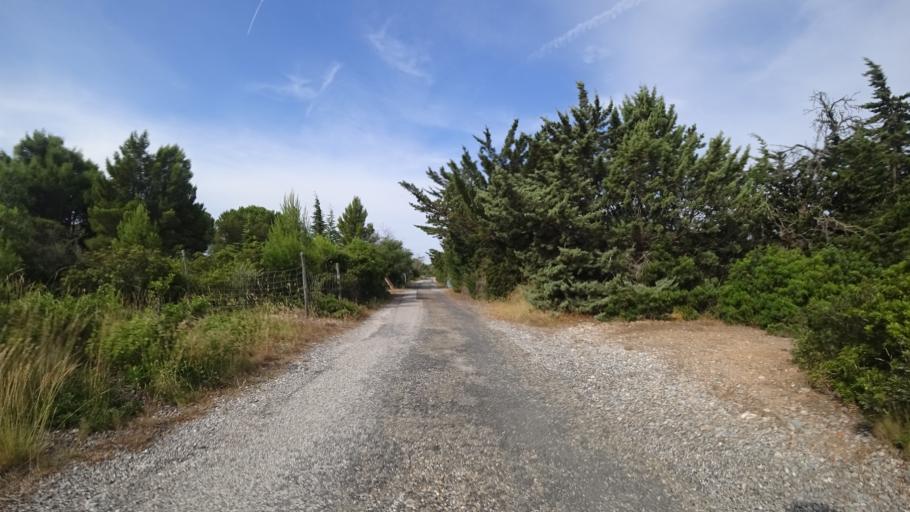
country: FR
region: Languedoc-Roussillon
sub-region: Departement de l'Aude
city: Leucate
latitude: 42.8994
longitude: 3.0286
